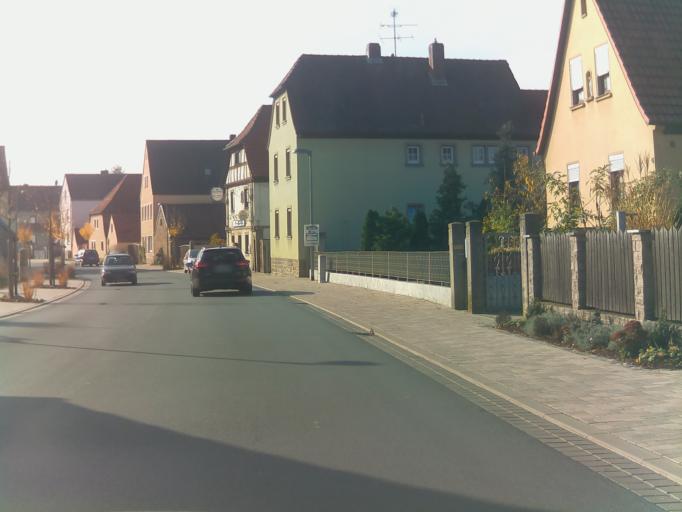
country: DE
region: Bavaria
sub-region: Regierungsbezirk Unterfranken
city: Kleinlangheim
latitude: 49.8150
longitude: 10.2925
